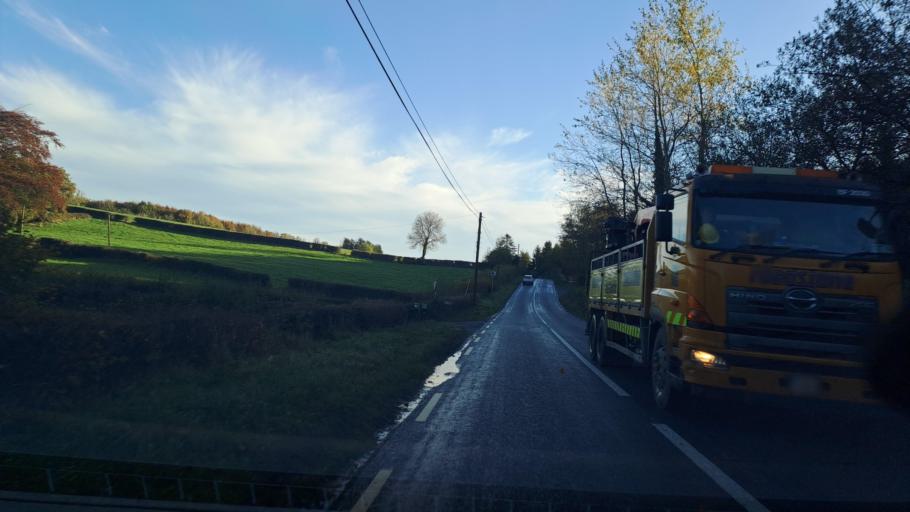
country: IE
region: Ulster
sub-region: An Cabhan
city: Cootehill
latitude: 54.1119
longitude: -7.0452
